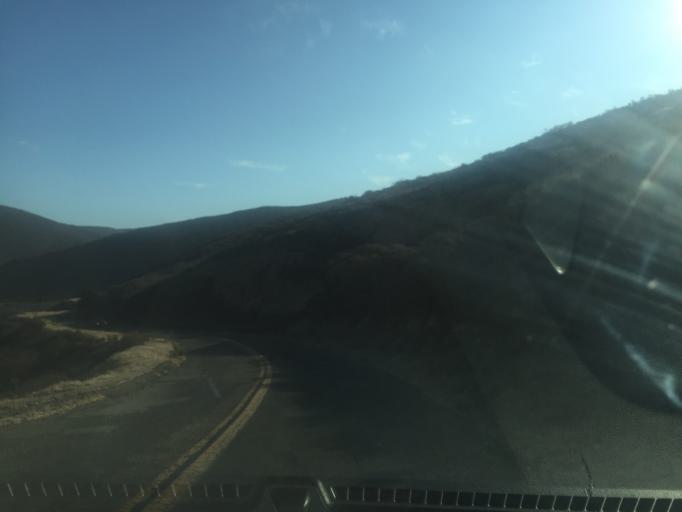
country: US
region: California
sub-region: Santa Barbara County
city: Lompoc
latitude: 34.5093
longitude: -120.4943
